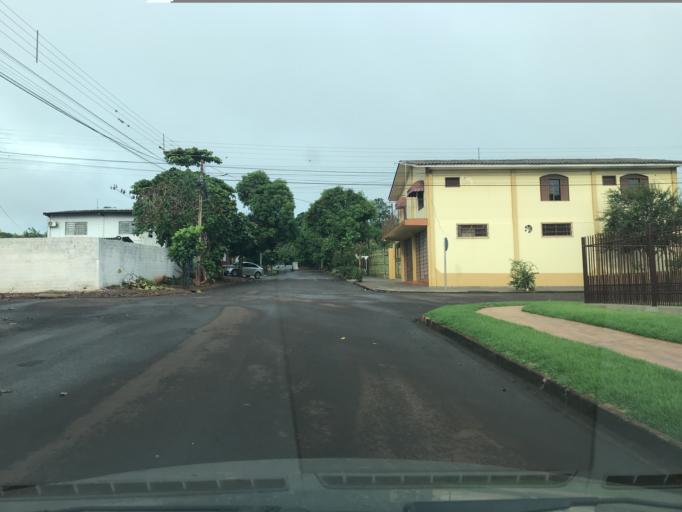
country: BR
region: Parana
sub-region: Palotina
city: Palotina
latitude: -24.2928
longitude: -53.8471
